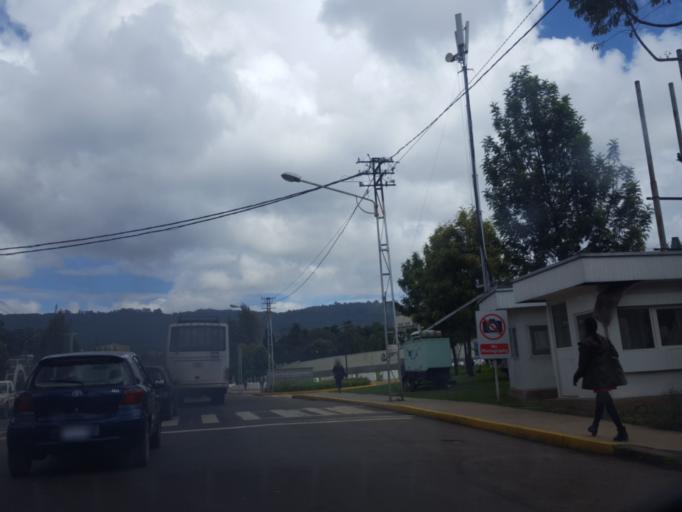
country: ET
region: Adis Abeba
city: Addis Ababa
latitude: 9.0568
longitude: 38.7628
